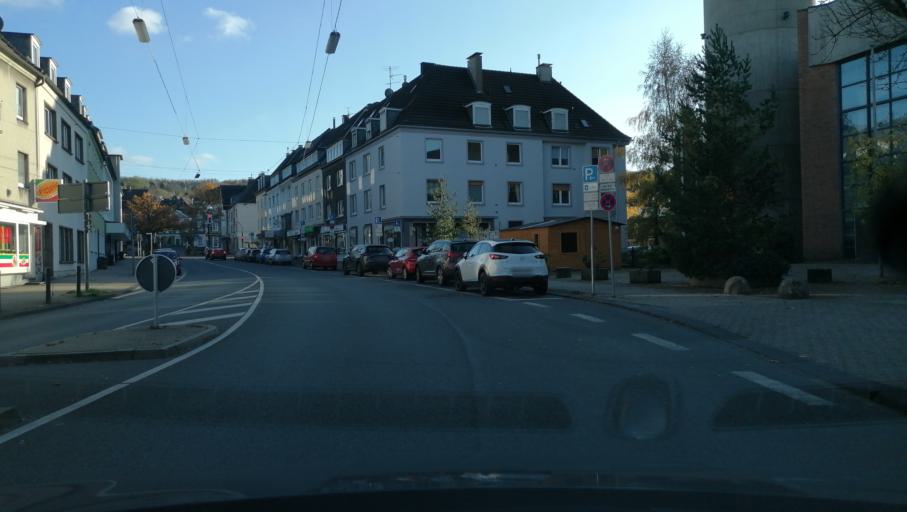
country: DE
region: North Rhine-Westphalia
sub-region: Regierungsbezirk Arnsberg
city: Schwelm
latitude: 51.2851
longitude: 7.2906
